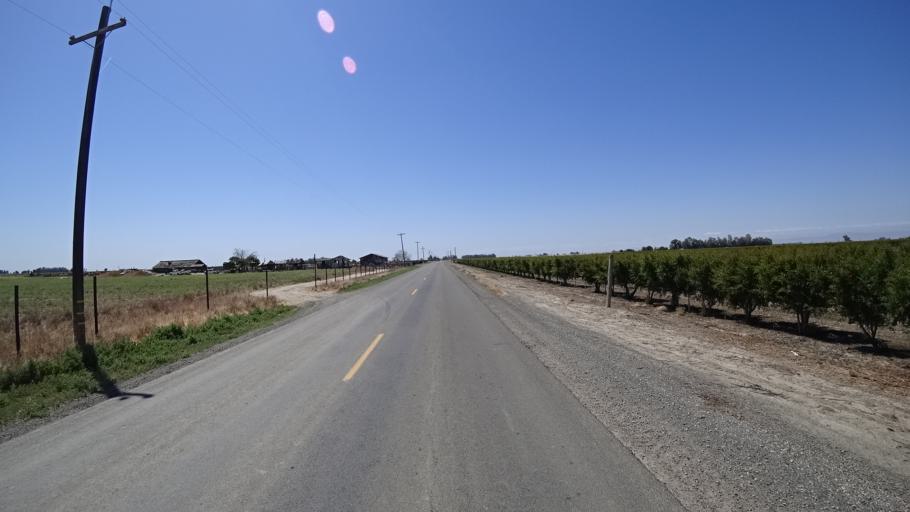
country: US
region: California
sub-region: Kings County
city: Stratford
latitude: 36.2179
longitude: -119.7982
